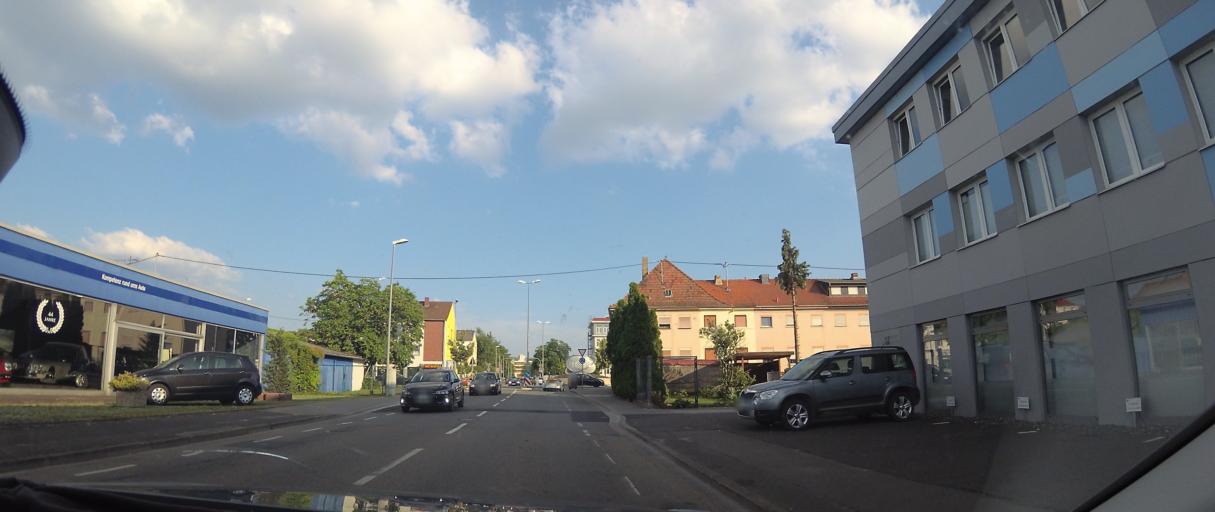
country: DE
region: Rheinland-Pfalz
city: Bad Kreuznach
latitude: 49.8450
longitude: 7.8762
